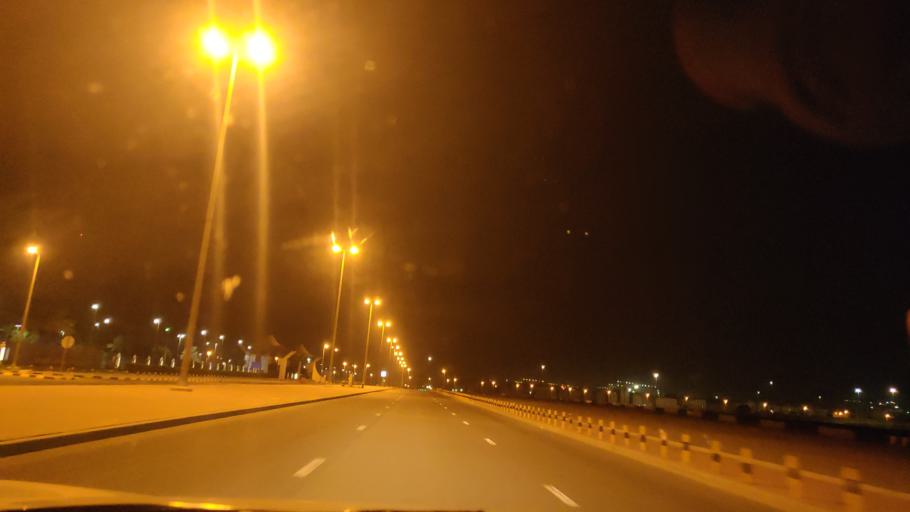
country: KW
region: Al Asimah
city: Ar Rabiyah
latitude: 29.2734
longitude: 47.9157
